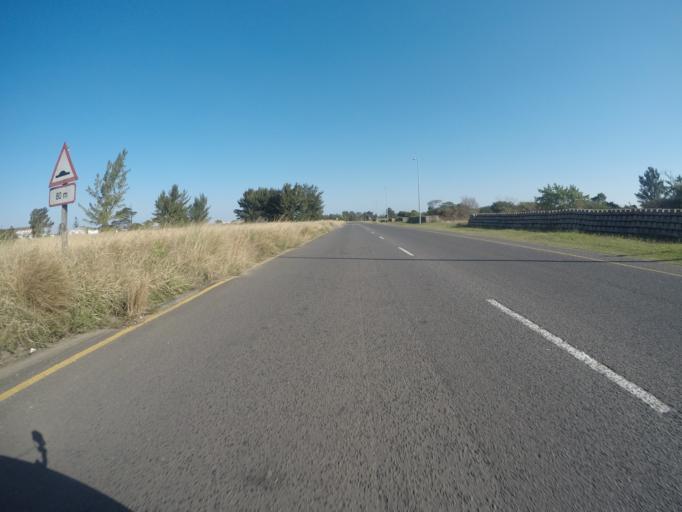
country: ZA
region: KwaZulu-Natal
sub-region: uThungulu District Municipality
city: Richards Bay
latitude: -28.7902
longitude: 32.0783
